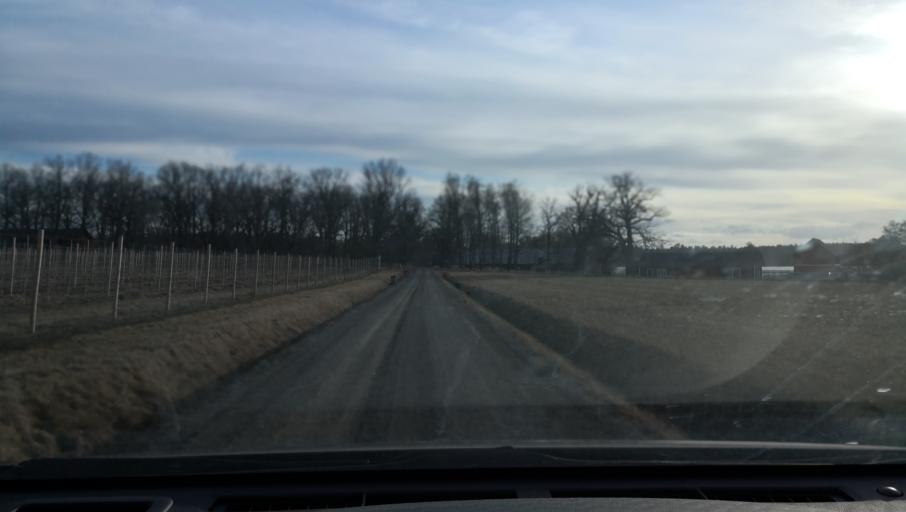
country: SE
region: Uppsala
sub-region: Enkopings Kommun
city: Dalby
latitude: 59.4771
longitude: 17.2529
